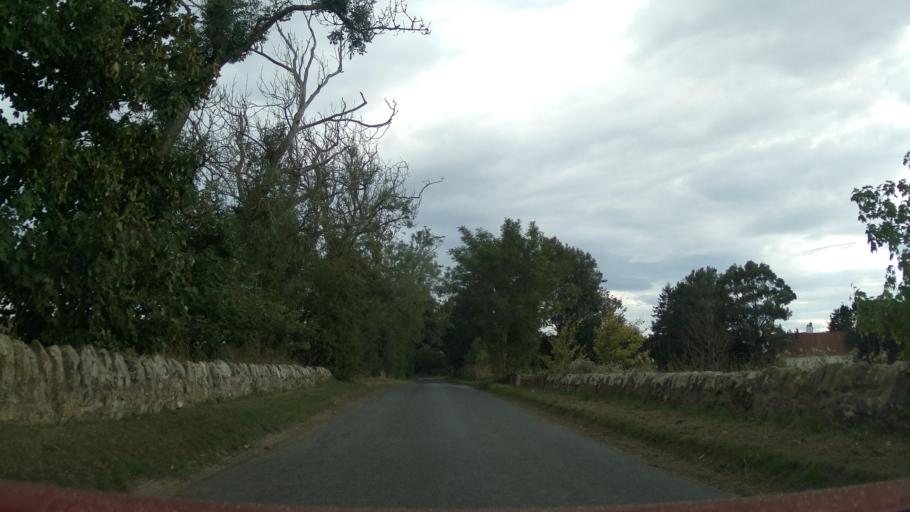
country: GB
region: Scotland
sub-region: Fife
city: Saint Andrews
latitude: 56.3160
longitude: -2.7798
